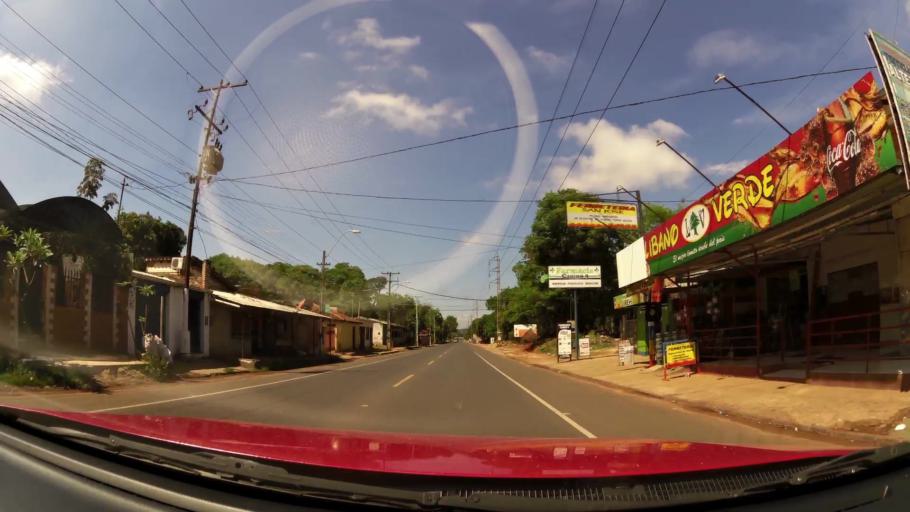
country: PY
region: Central
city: San Lorenzo
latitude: -25.3242
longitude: -57.5090
